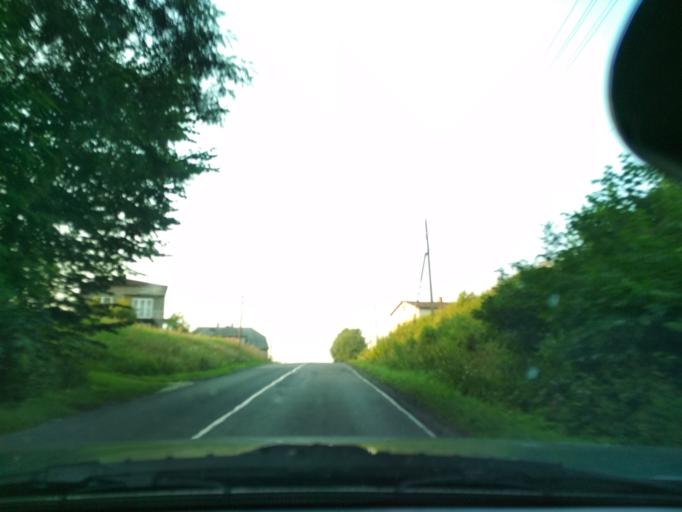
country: PL
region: Lesser Poland Voivodeship
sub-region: Powiat olkuski
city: Wolbrom
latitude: 50.4006
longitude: 19.7658
